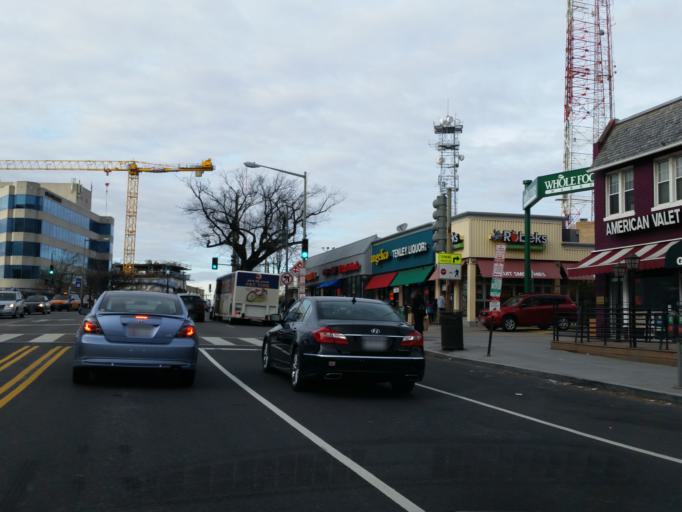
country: US
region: Maryland
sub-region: Montgomery County
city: Friendship Village
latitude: 38.9483
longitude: -77.0798
